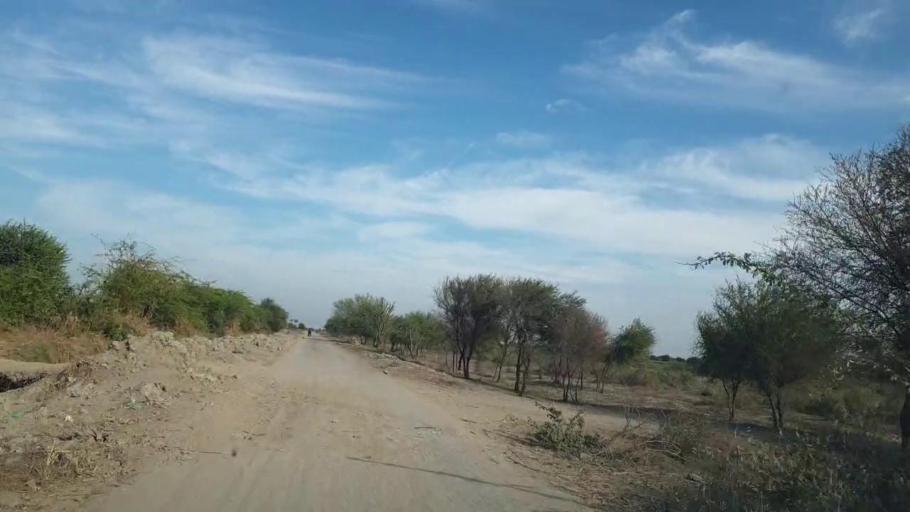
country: PK
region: Sindh
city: Pithoro
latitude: 25.6457
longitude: 69.3552
